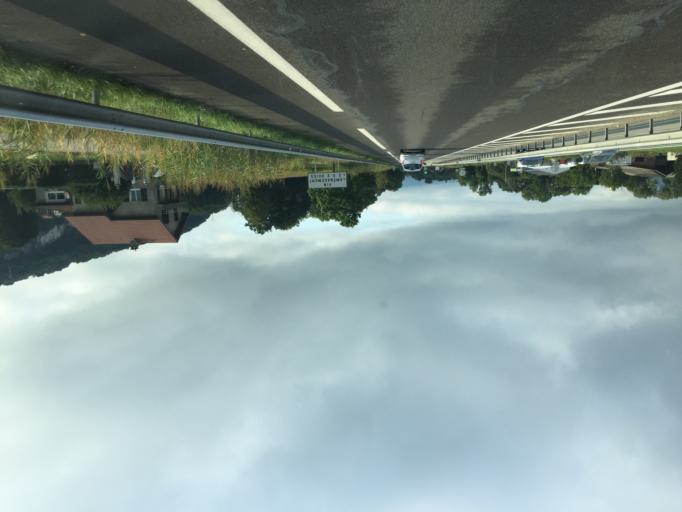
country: FR
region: Rhone-Alpes
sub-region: Departement de la Savoie
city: Voglans
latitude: 45.6292
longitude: 5.8917
